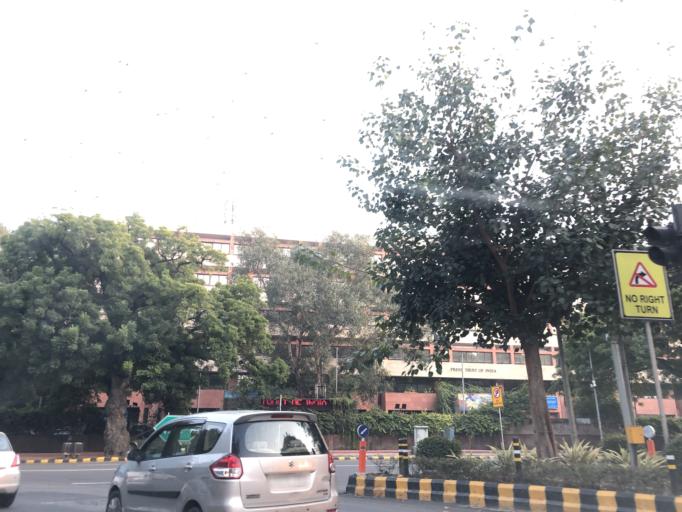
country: IN
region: NCT
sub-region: New Delhi
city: New Delhi
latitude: 28.6205
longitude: 77.2103
